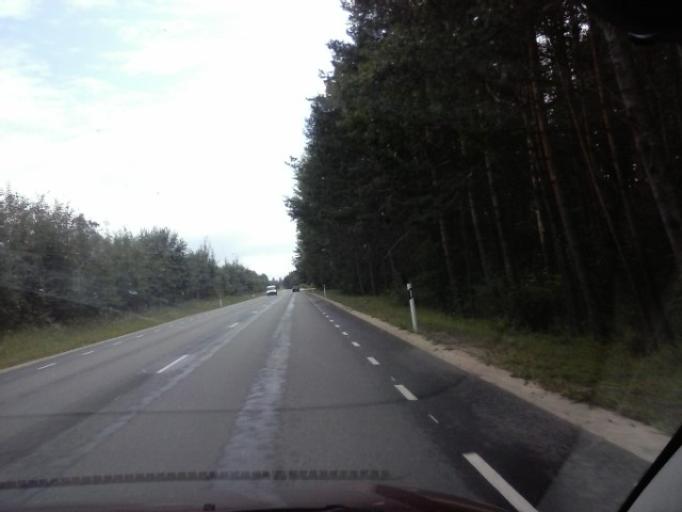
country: EE
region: Tartu
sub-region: UElenurme vald
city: Ulenurme
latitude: 58.3219
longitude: 26.9836
